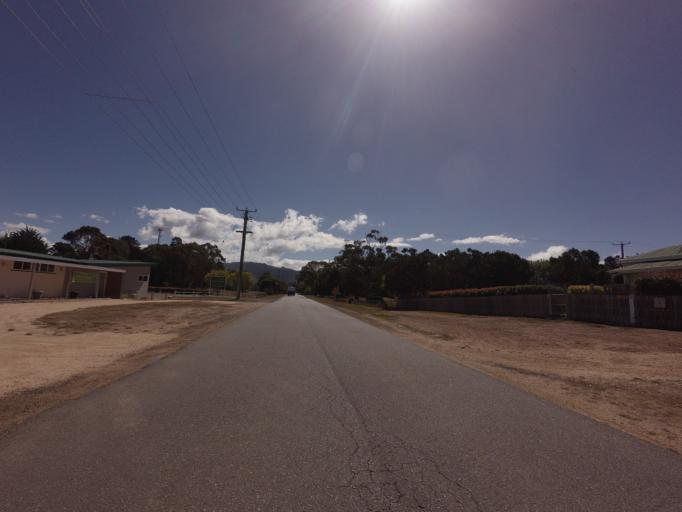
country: AU
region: Tasmania
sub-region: Break O'Day
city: St Helens
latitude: -41.5863
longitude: 148.1878
